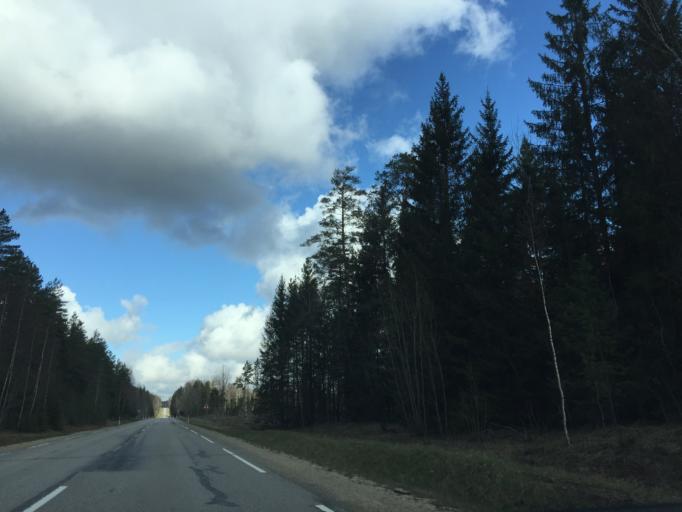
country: LV
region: Apes Novads
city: Ape
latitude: 57.5090
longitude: 26.7776
